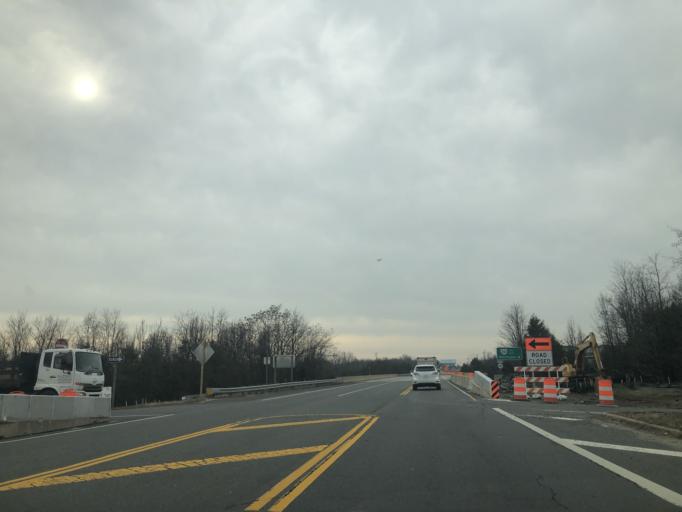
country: US
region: Virginia
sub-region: Loudoun County
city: Broadlands
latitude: 39.0382
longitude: -77.5223
